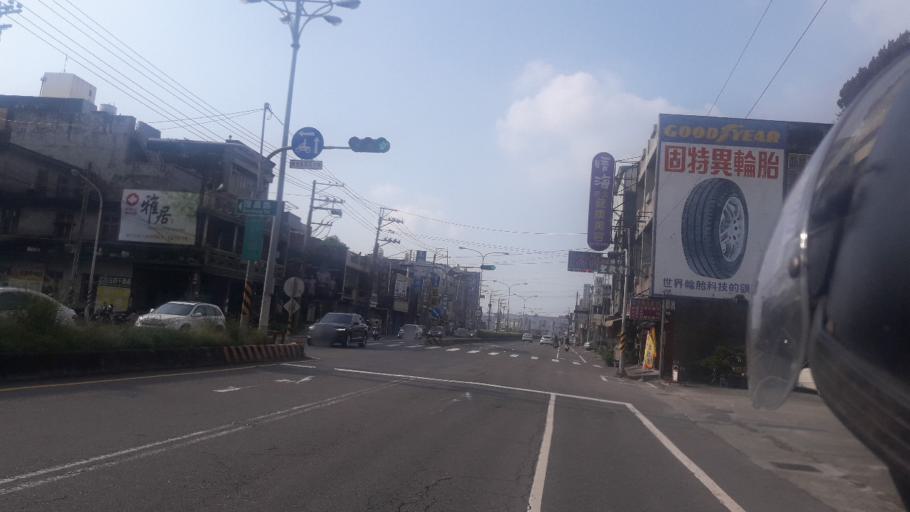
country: TW
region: Taiwan
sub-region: Tainan
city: Tainan
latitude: 22.8619
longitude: 120.2586
